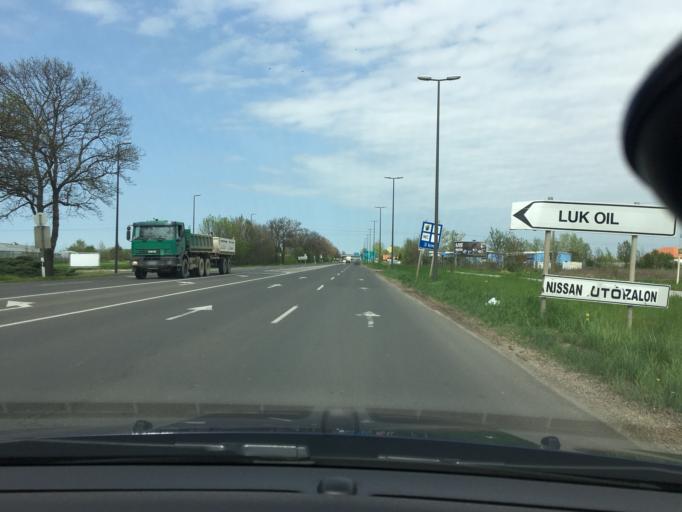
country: HU
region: Csongrad
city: Szeged
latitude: 46.2890
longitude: 20.1734
